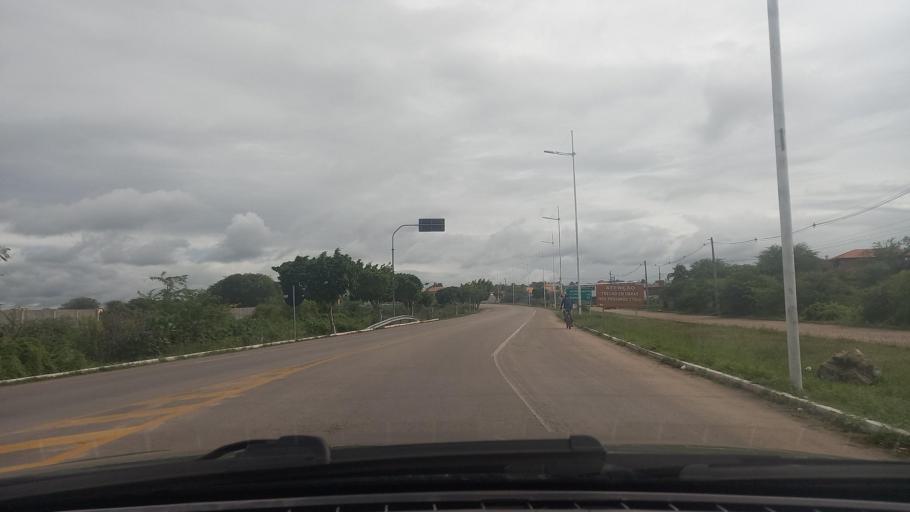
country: BR
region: Bahia
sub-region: Paulo Afonso
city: Paulo Afonso
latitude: -9.4384
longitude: -38.2050
